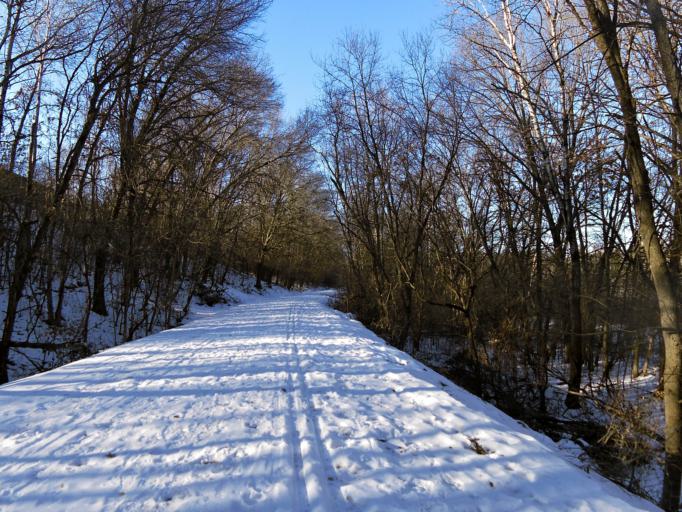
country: US
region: Minnesota
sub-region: Washington County
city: Grant
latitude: 45.0747
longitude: -92.8749
